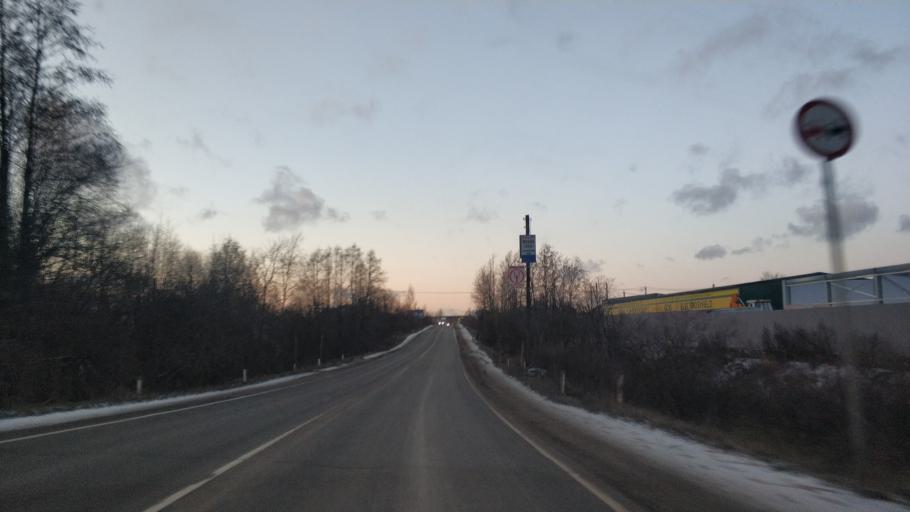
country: RU
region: St.-Petersburg
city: Pontonnyy
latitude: 59.8089
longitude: 30.6143
